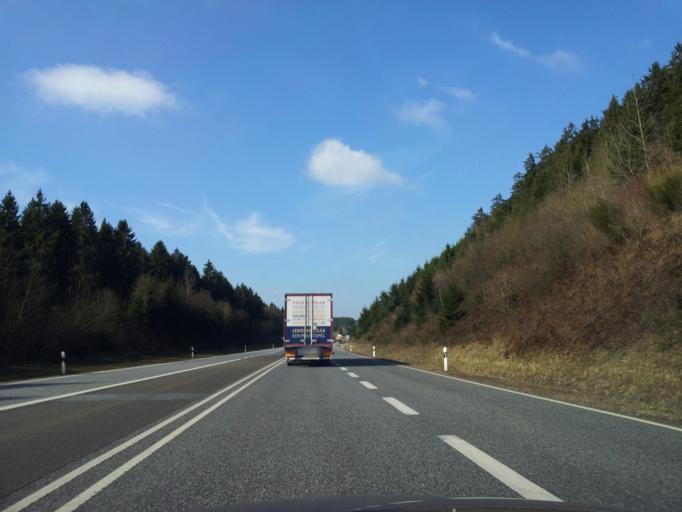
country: DE
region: Rheinland-Pfalz
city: Pittenbach
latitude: 50.2037
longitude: 6.3372
